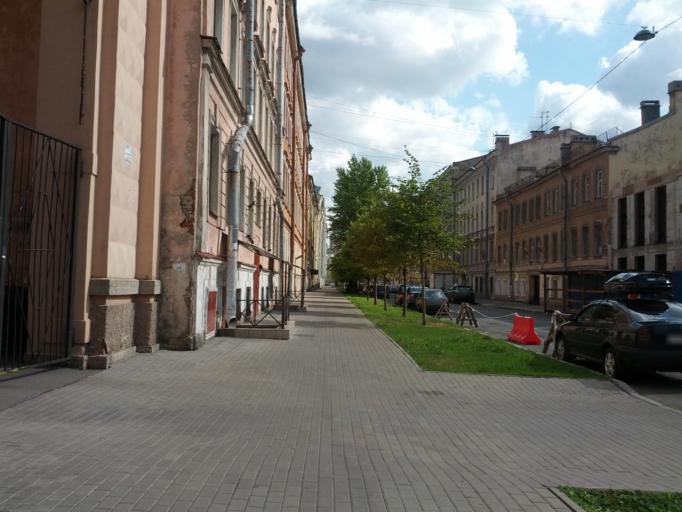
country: RU
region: St.-Petersburg
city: Saint Petersburg
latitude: 59.9145
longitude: 30.3106
